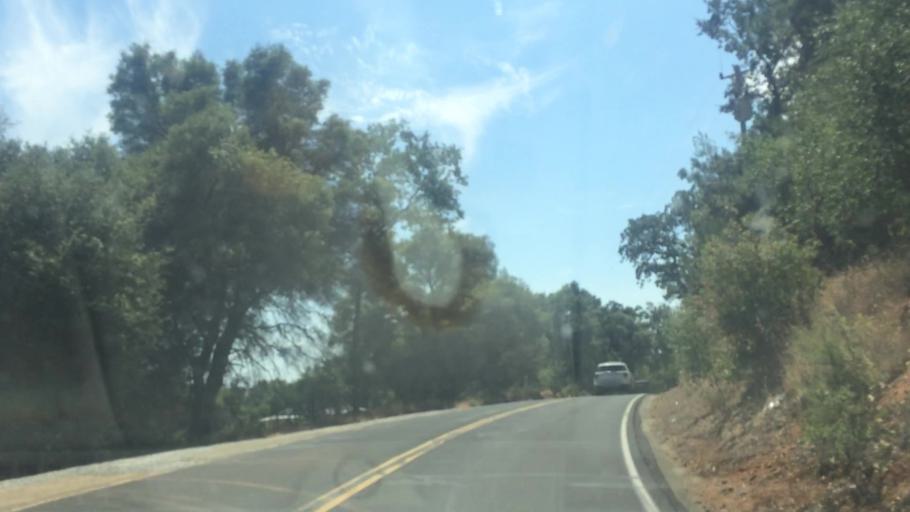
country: US
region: California
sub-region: Amador County
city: Pine Grove
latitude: 38.4061
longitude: -120.7135
